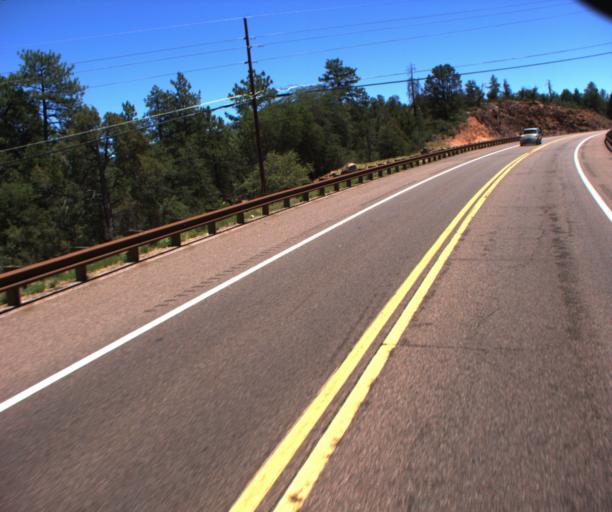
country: US
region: Arizona
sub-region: Gila County
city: Payson
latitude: 34.2774
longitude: -111.3226
